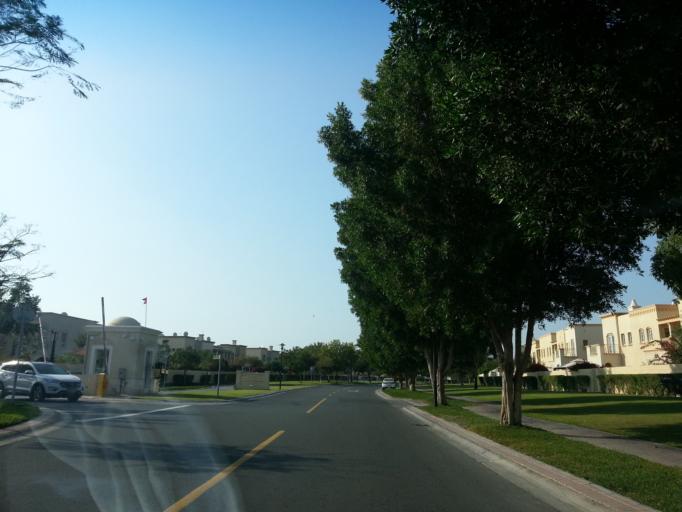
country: AE
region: Dubai
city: Dubai
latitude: 25.0521
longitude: 55.1825
